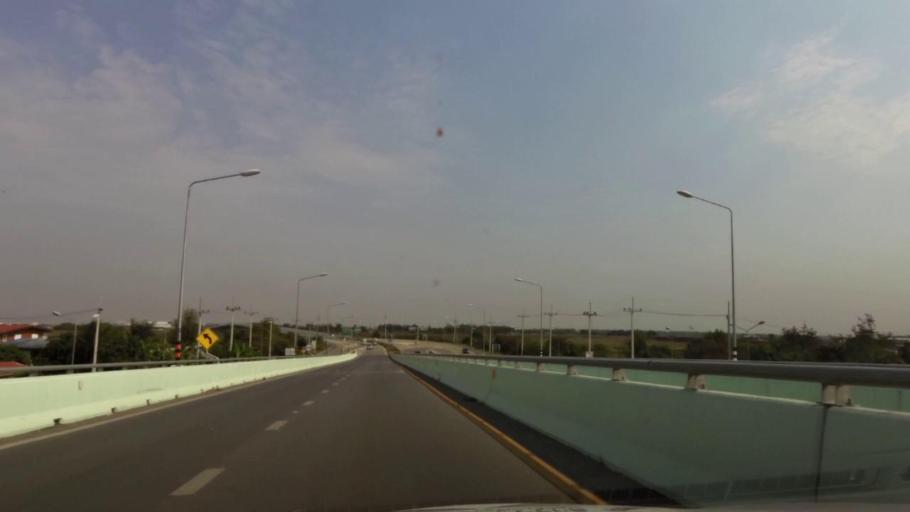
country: TH
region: Phra Nakhon Si Ayutthaya
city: Phra Nakhon Si Ayutthaya
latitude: 14.3307
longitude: 100.5771
